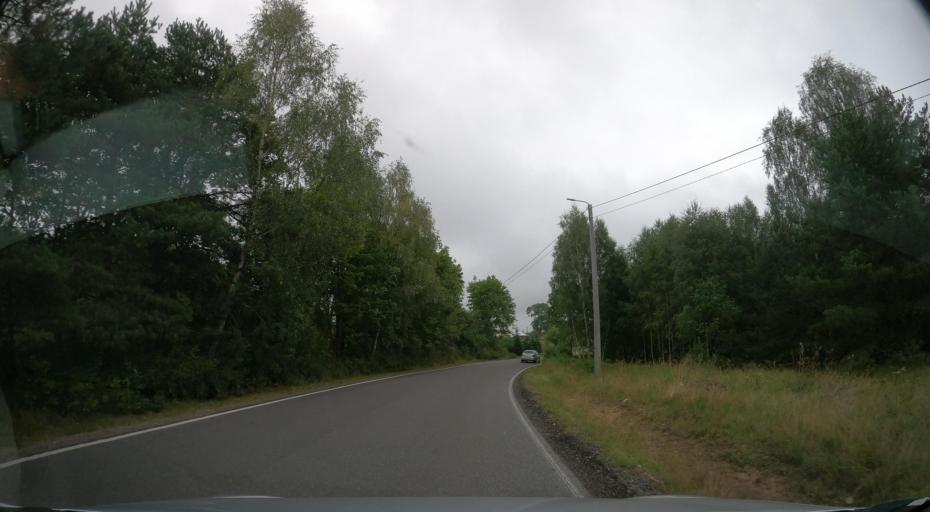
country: PL
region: Pomeranian Voivodeship
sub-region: Powiat wejherowski
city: Leczyce
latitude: 54.4982
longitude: 17.8418
